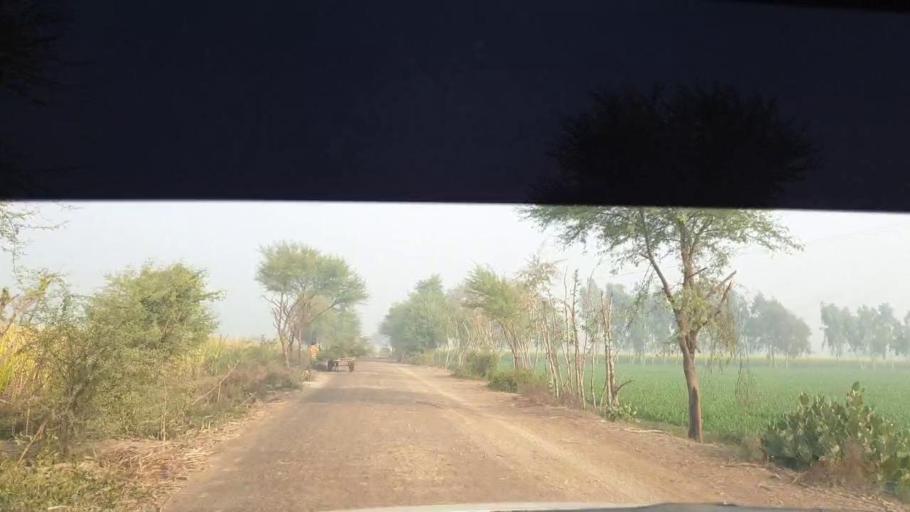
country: PK
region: Sindh
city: Berani
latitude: 25.7872
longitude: 68.7716
